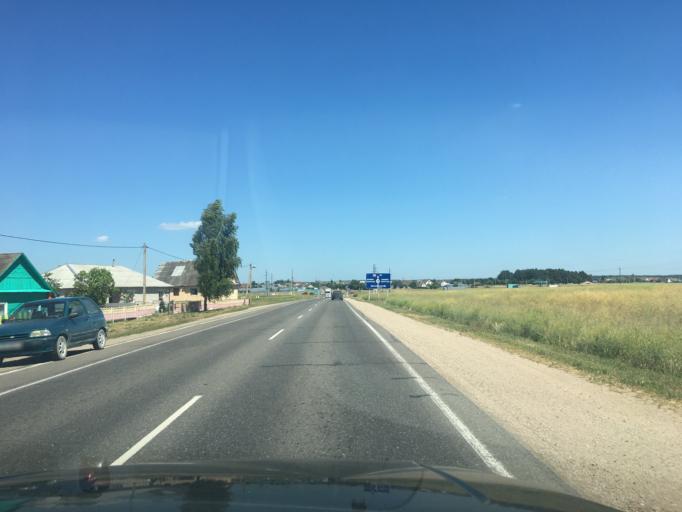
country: BY
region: Grodnenskaya
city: Iwye
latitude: 53.9119
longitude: 25.7633
